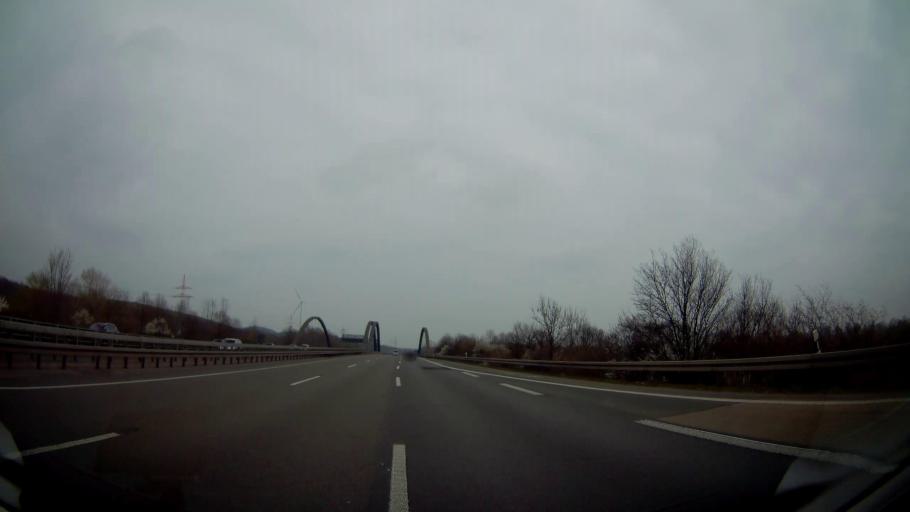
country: DE
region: North Rhine-Westphalia
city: Waltrop
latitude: 51.5831
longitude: 7.4053
